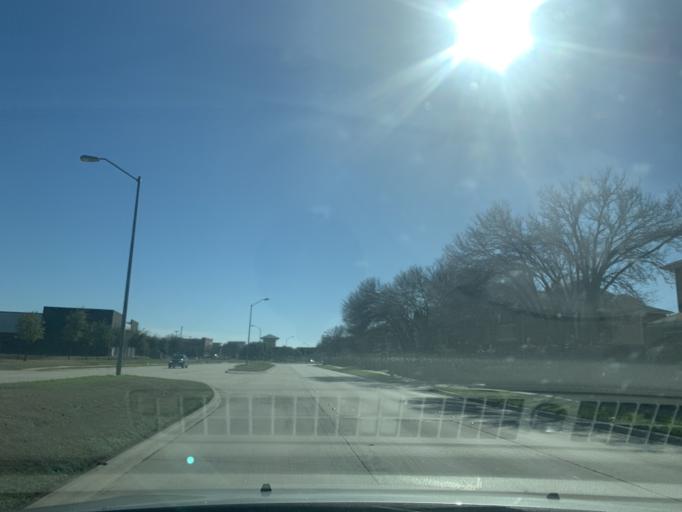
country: US
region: Texas
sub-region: Denton County
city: The Colony
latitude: 33.0588
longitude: -96.8329
